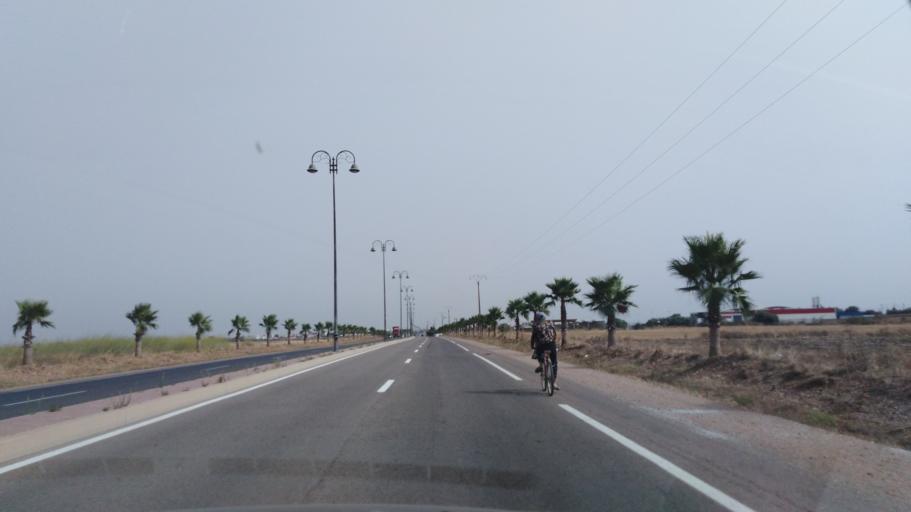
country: MA
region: Chaouia-Ouardigha
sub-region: Settat Province
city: Berrechid
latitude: 33.3020
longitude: -7.5995
